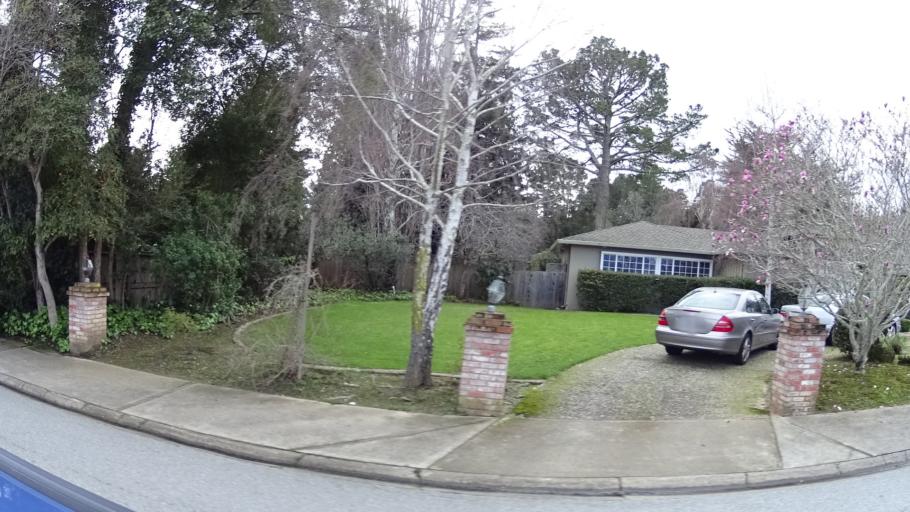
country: US
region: California
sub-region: San Mateo County
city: Hillsborough
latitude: 37.5526
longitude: -122.3721
